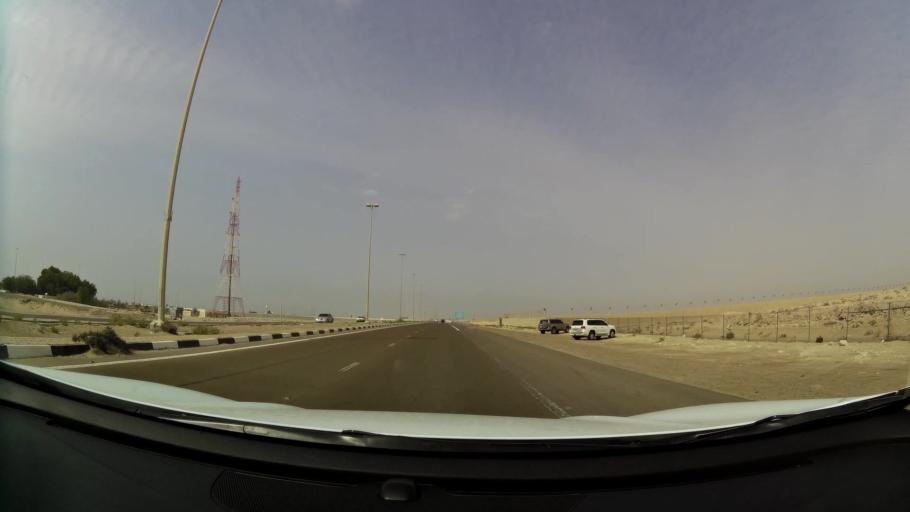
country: AE
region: Abu Dhabi
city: Abu Dhabi
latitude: 24.5579
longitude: 54.6987
